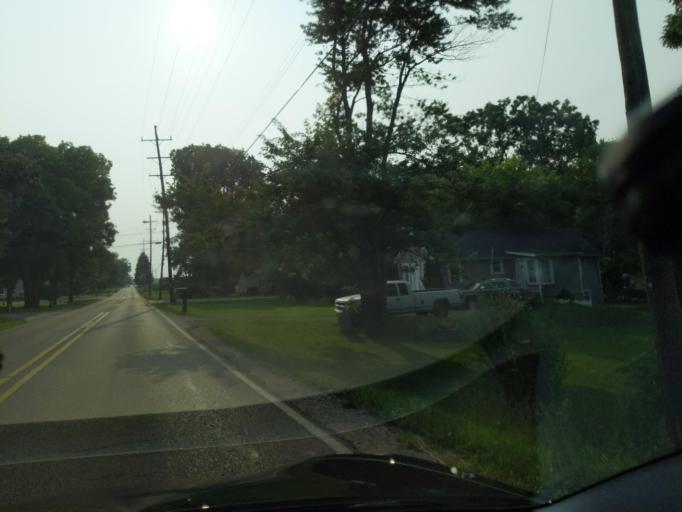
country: US
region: Michigan
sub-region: Jackson County
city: Jackson
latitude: 42.2620
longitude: -84.4387
